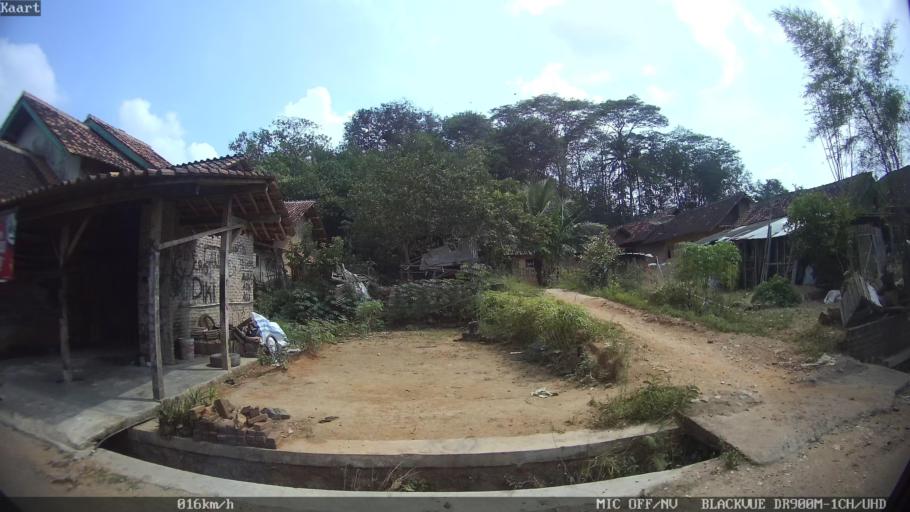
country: ID
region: Lampung
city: Pringsewu
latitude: -5.3600
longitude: 104.9633
